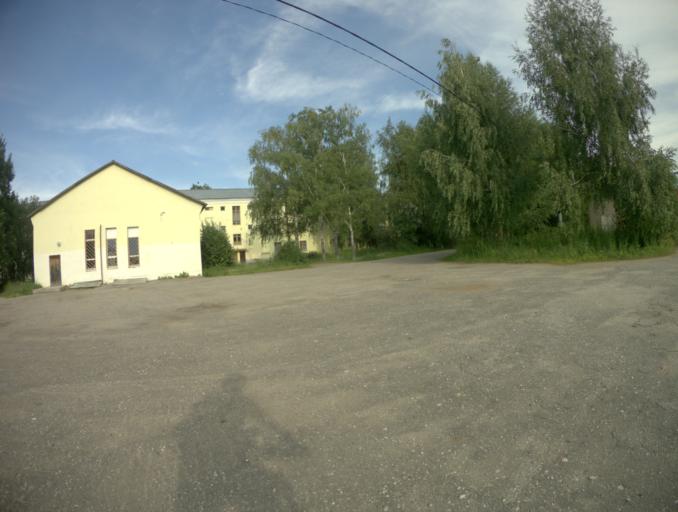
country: RU
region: Vladimir
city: Suzdal'
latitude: 56.4269
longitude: 40.4442
